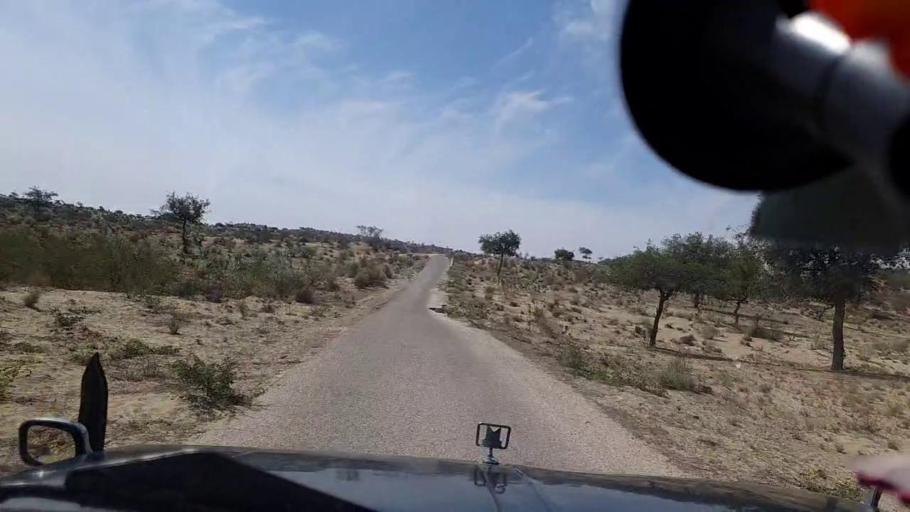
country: PK
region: Sindh
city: Diplo
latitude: 24.3909
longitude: 69.5891
